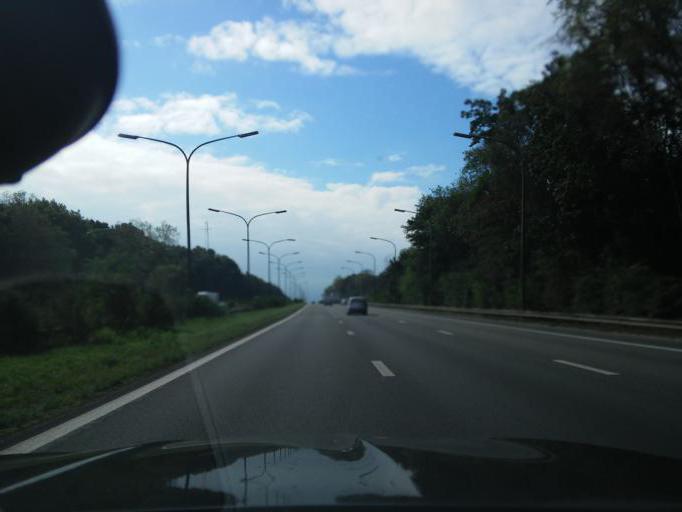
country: BE
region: Flanders
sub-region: Provincie Vlaams-Brabant
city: Beersel
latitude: 50.7632
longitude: 4.2905
